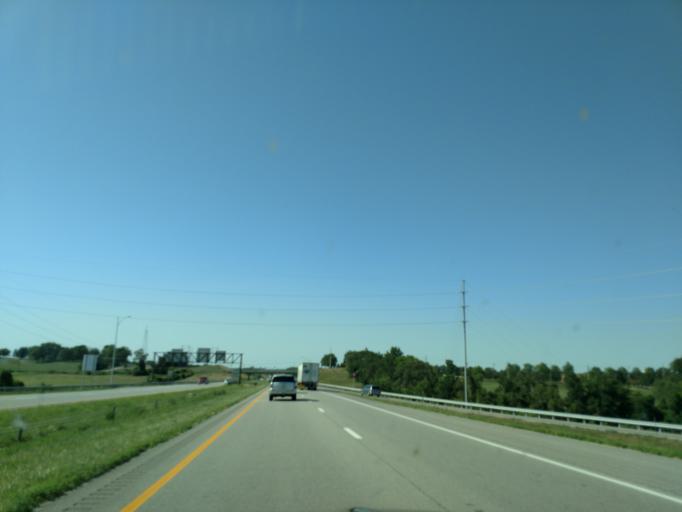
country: US
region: Missouri
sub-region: Buchanan County
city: Saint Joseph
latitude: 39.7510
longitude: -94.7897
